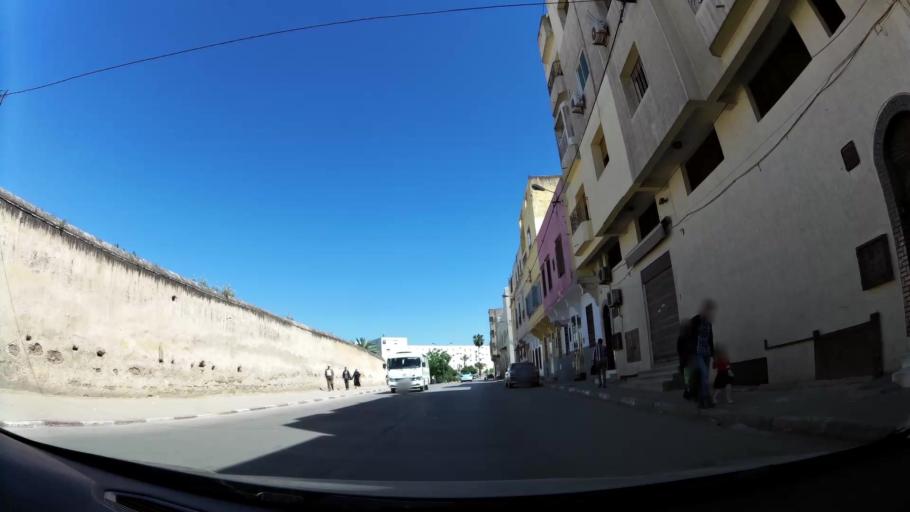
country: MA
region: Meknes-Tafilalet
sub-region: Meknes
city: Meknes
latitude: 33.8903
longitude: -5.5709
